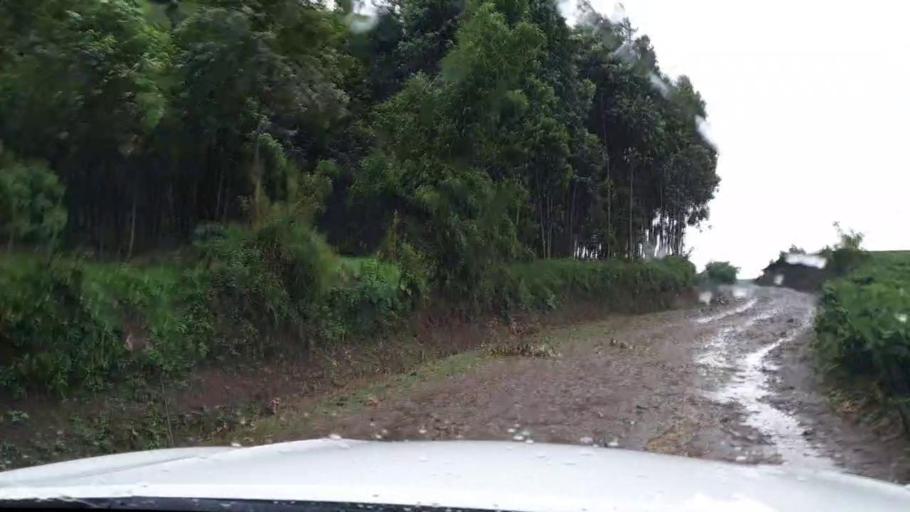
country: RW
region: Western Province
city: Cyangugu
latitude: -2.4619
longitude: 29.0363
